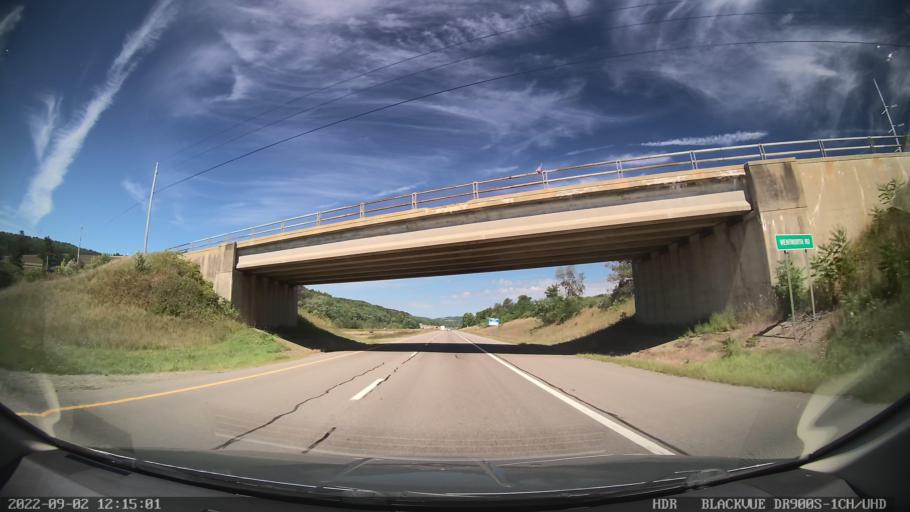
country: US
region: New York
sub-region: Steuben County
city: Wayland
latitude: 42.4613
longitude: -77.4820
